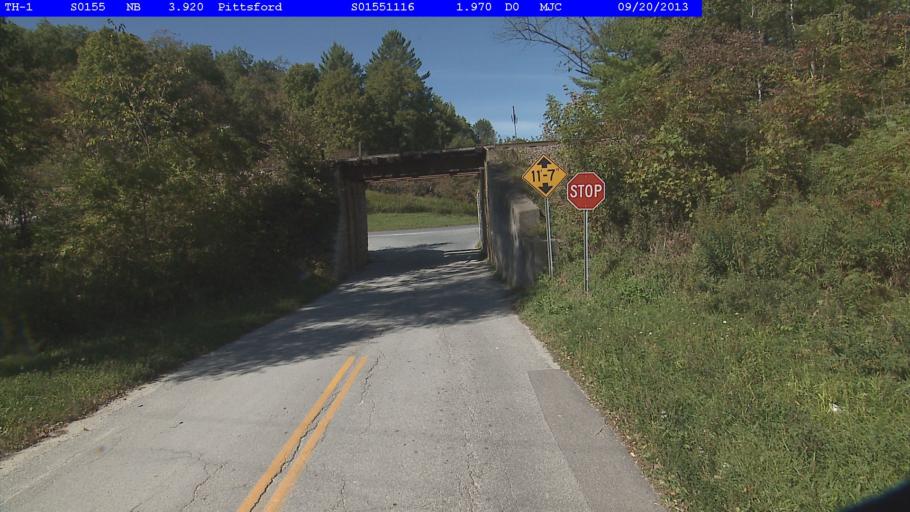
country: US
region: Vermont
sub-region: Rutland County
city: Brandon
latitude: 43.7162
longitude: -73.0604
